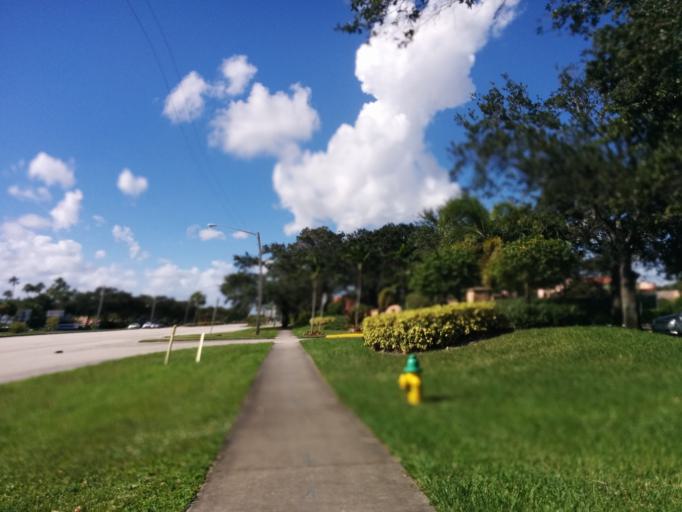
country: US
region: Florida
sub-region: Broward County
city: Pine Island Ridge
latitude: 26.0848
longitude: -80.2506
